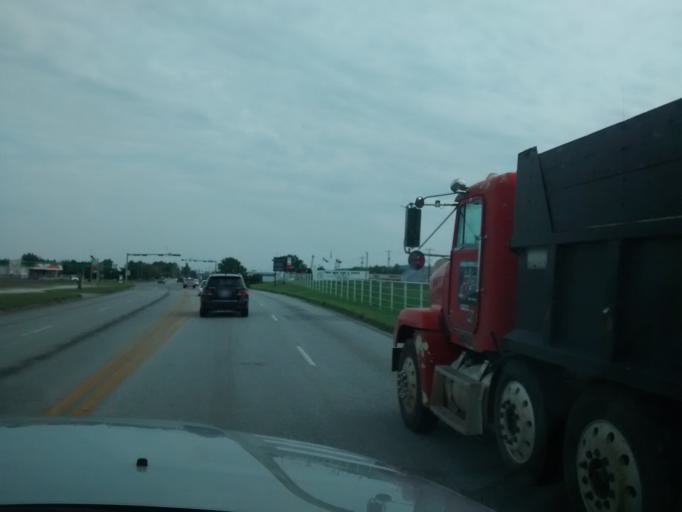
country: US
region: Arkansas
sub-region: Washington County
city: Springdale
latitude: 36.1831
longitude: -94.1162
